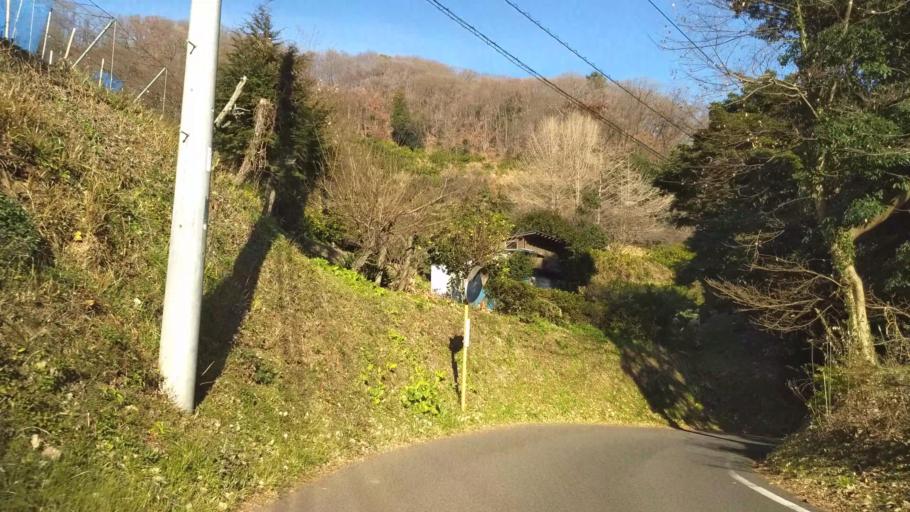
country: JP
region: Kanagawa
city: Hadano
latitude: 35.3725
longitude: 139.2472
